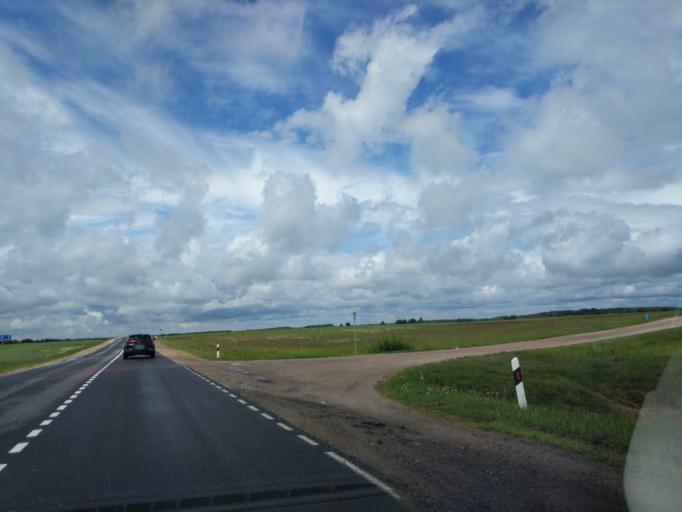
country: BY
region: Minsk
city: Il'ya
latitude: 54.3886
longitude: 27.3546
